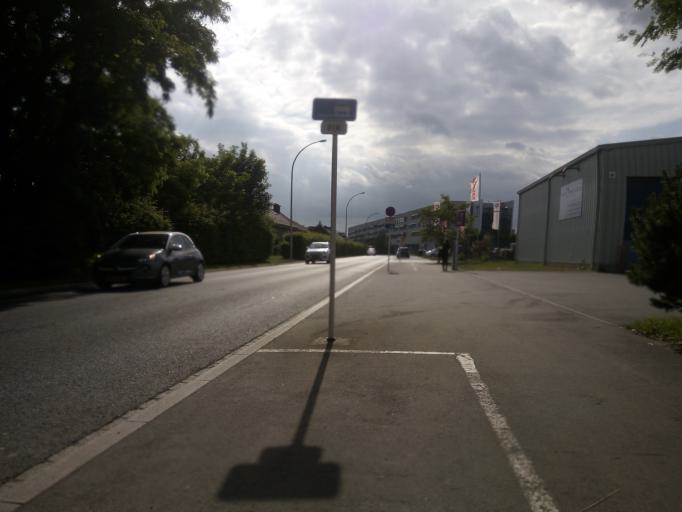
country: LU
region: Luxembourg
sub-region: Canton d'Esch-sur-Alzette
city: Esch-sur-Alzette
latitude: 49.5099
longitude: 5.9706
